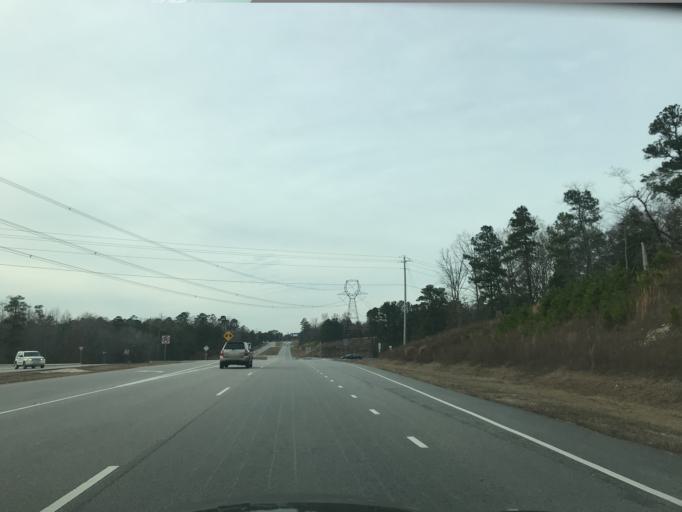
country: US
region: North Carolina
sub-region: Wake County
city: Rolesville
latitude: 35.9000
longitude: -78.4777
